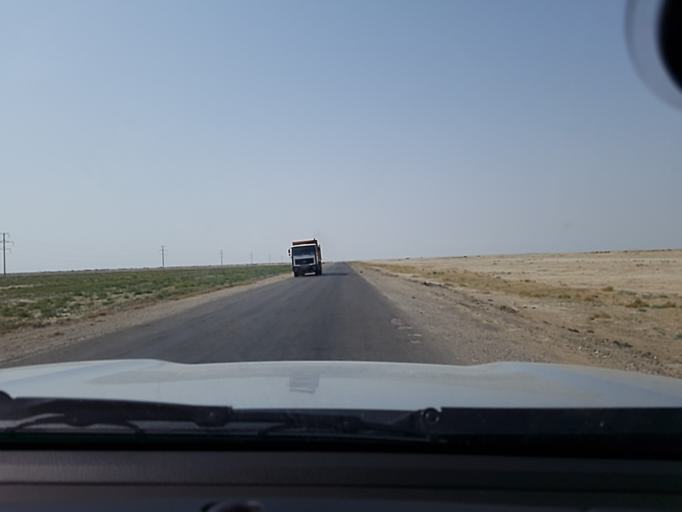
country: TM
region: Balkan
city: Gumdag
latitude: 38.8549
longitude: 54.5952
